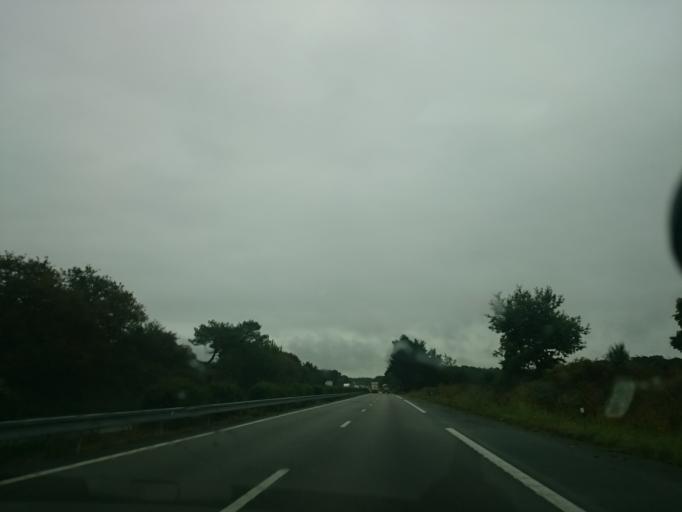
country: FR
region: Brittany
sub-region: Departement du Morbihan
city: Theix
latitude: 47.6166
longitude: -2.6223
